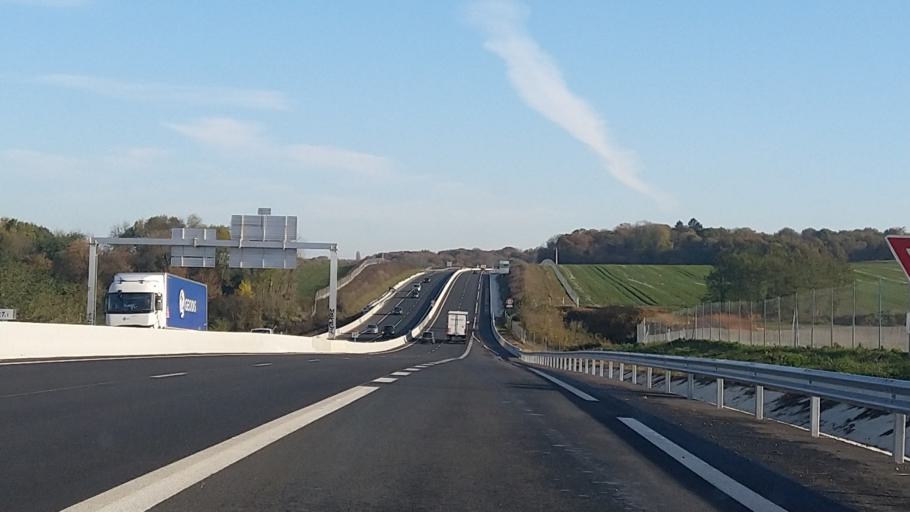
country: FR
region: Ile-de-France
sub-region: Departement du Val-d'Oise
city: Mours
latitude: 49.1005
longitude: 2.2793
